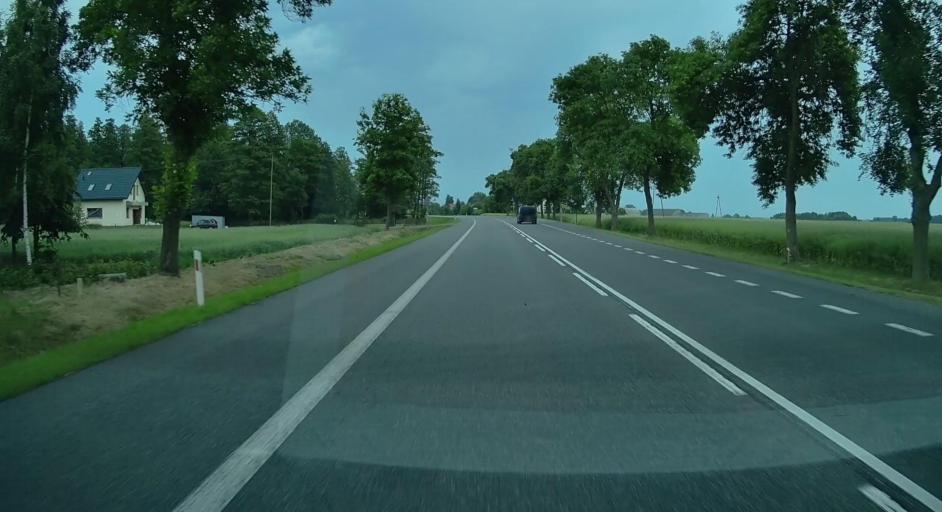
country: PL
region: Lublin Voivodeship
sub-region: Powiat lukowski
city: Trzebieszow
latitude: 52.0639
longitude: 22.5451
